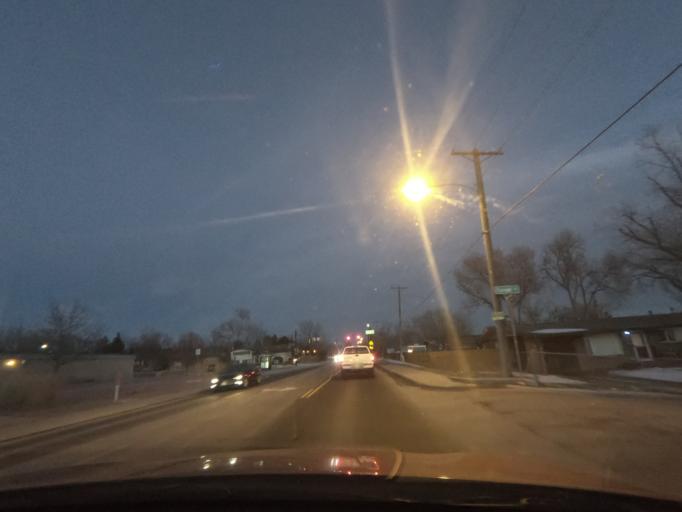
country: US
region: Colorado
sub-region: El Paso County
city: Security-Widefield
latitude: 38.7373
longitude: -104.7228
